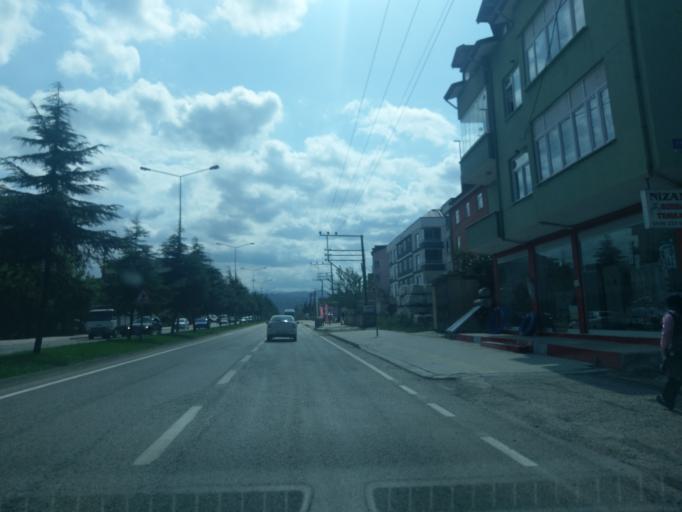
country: TR
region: Ordu
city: Ordu
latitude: 40.9607
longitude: 37.8981
